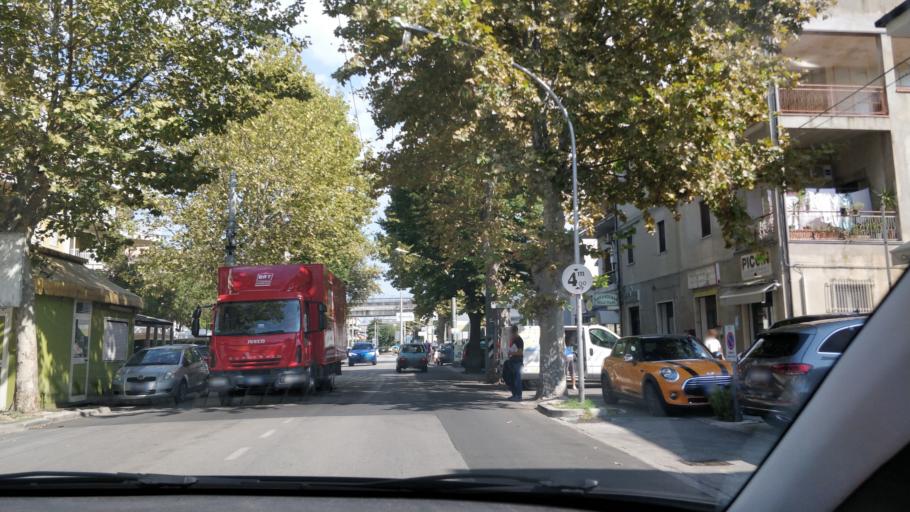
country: IT
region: Abruzzo
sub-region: Provincia di Chieti
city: Chieti
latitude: 42.3713
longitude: 14.1433
